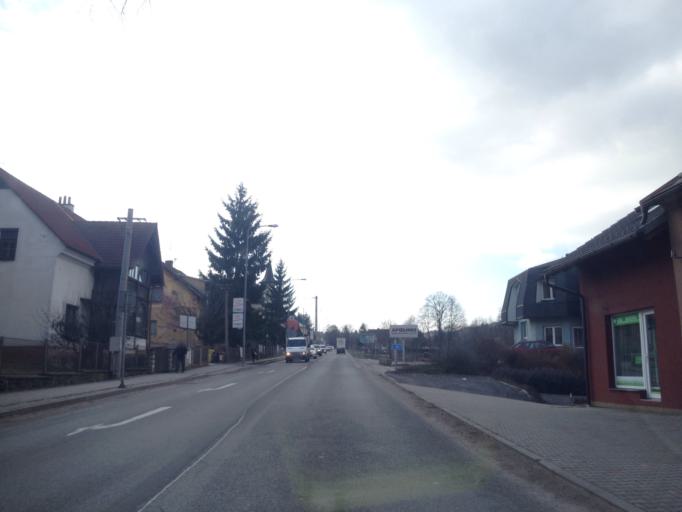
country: CZ
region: Kralovehradecky
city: Nova Paka
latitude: 50.4885
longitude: 15.5190
